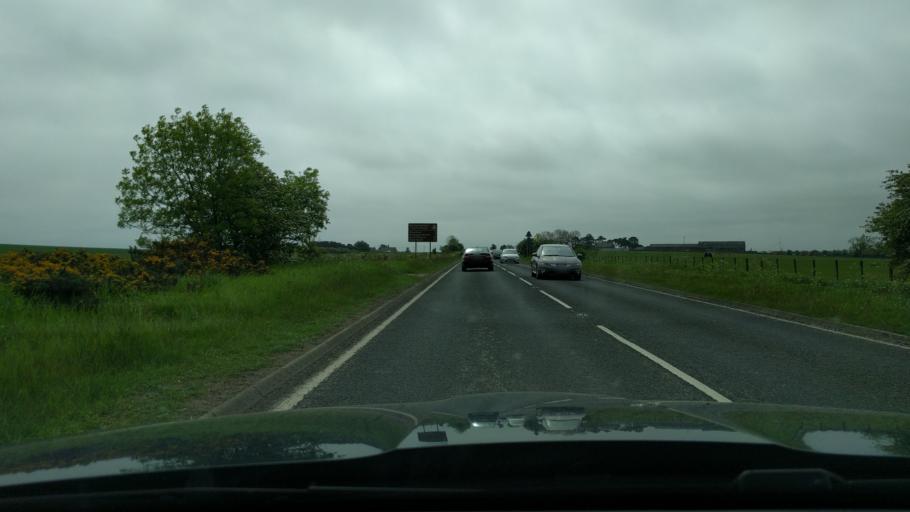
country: GB
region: England
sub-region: Northumberland
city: East Chevington
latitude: 55.2488
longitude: -1.6012
